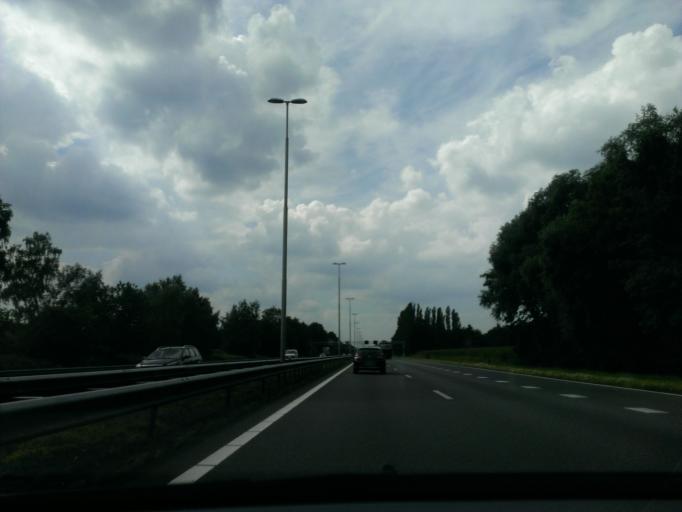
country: NL
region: Gelderland
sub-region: Gemeente Barneveld
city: Zwartebroek
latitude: 52.1656
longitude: 5.4749
